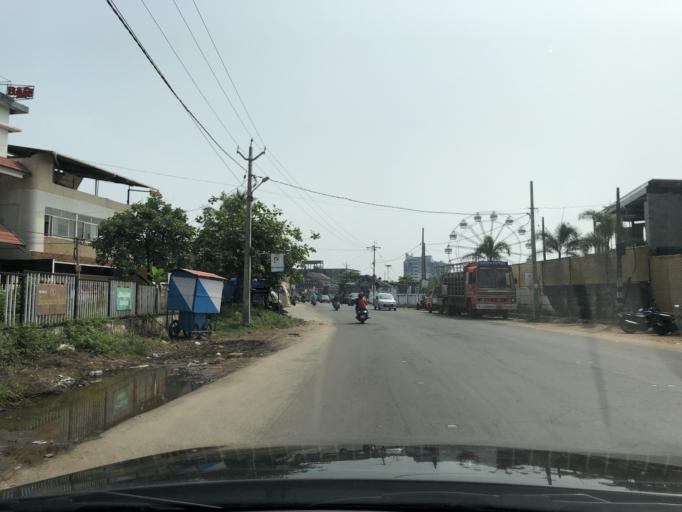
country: IN
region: Kerala
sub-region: Kozhikode
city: Kozhikode
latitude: 11.2514
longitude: 75.7705
